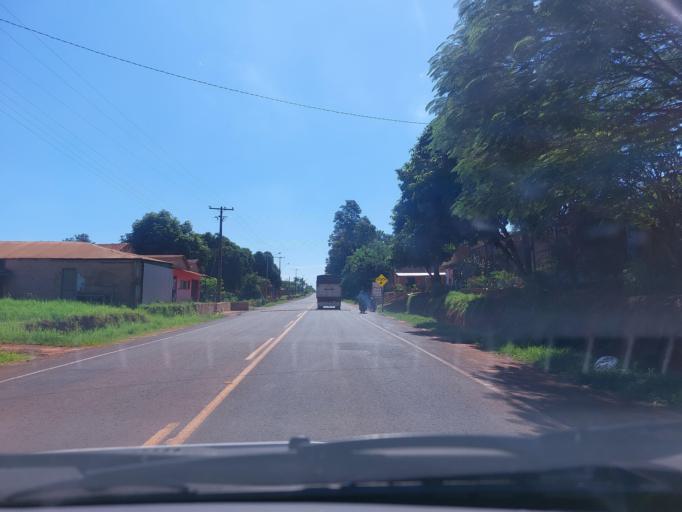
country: PY
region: San Pedro
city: Guayaybi
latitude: -24.5867
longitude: -56.5196
